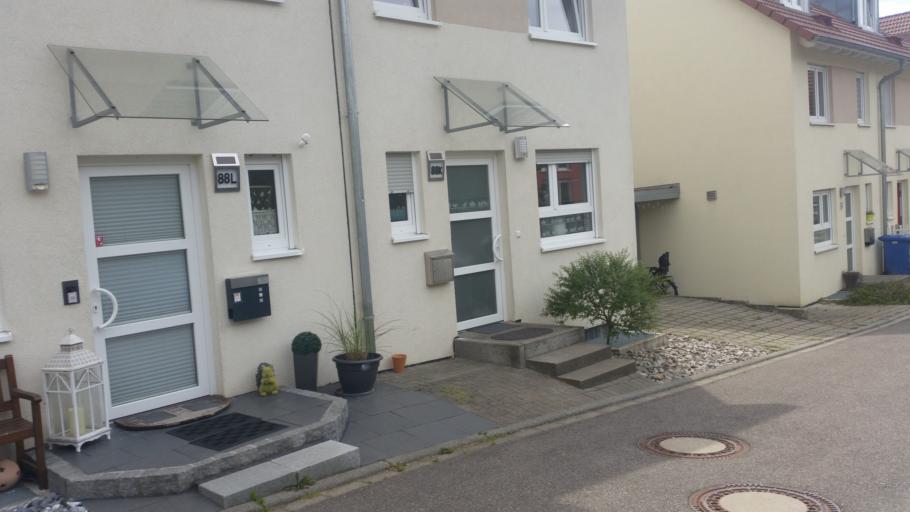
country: DE
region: Baden-Wuerttemberg
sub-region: Freiburg Region
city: Loerrach
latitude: 47.6093
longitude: 7.6721
